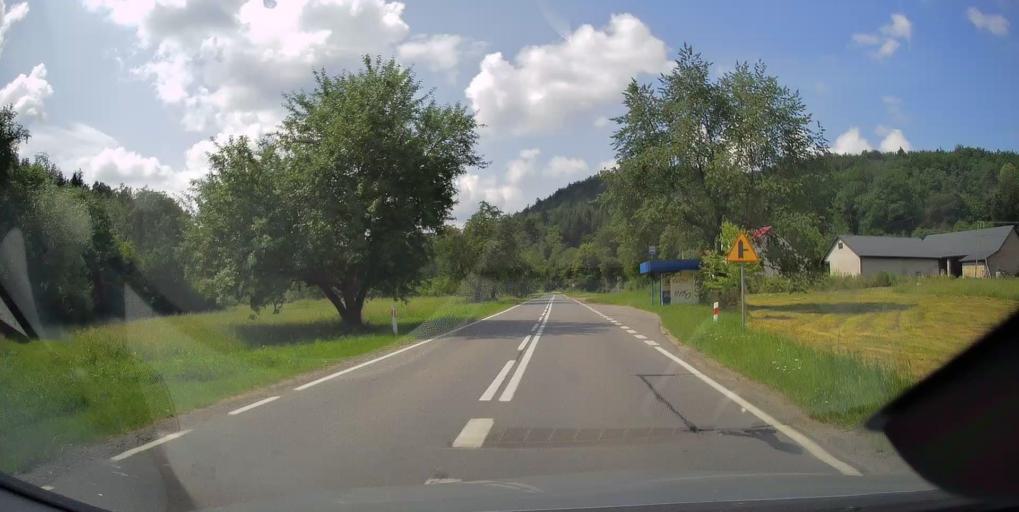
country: PL
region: Lesser Poland Voivodeship
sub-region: Powiat tarnowski
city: Zakliczyn
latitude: 49.8215
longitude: 20.8012
